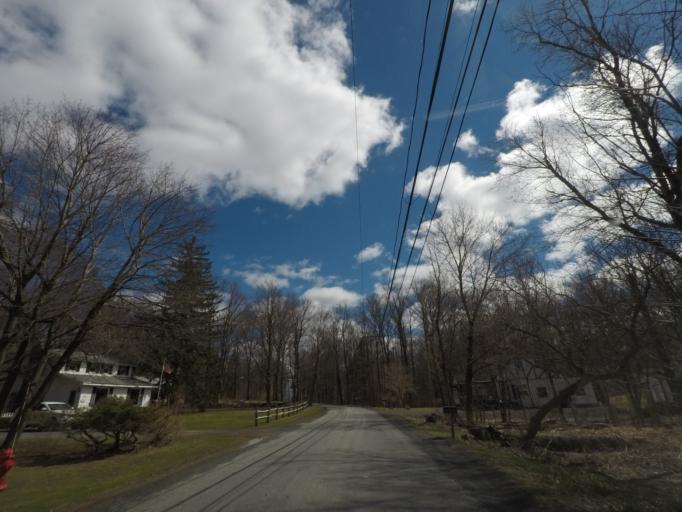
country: US
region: New York
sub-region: Albany County
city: Voorheesville
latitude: 42.6189
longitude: -73.9671
